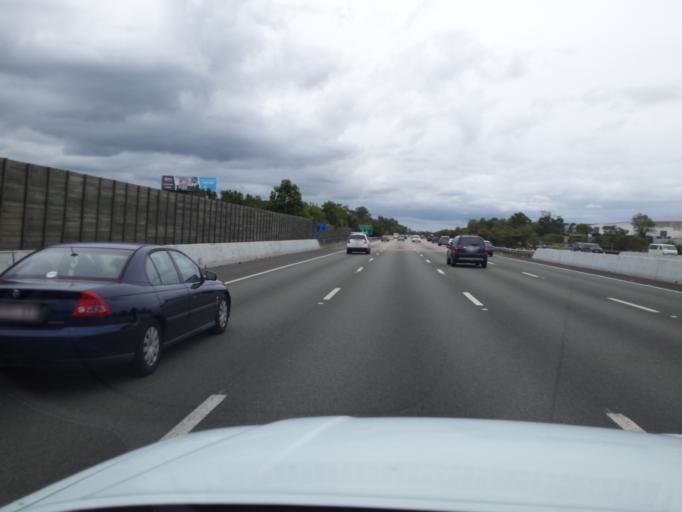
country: AU
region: Queensland
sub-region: Gold Coast
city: Nerang
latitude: -27.9418
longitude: 153.3377
